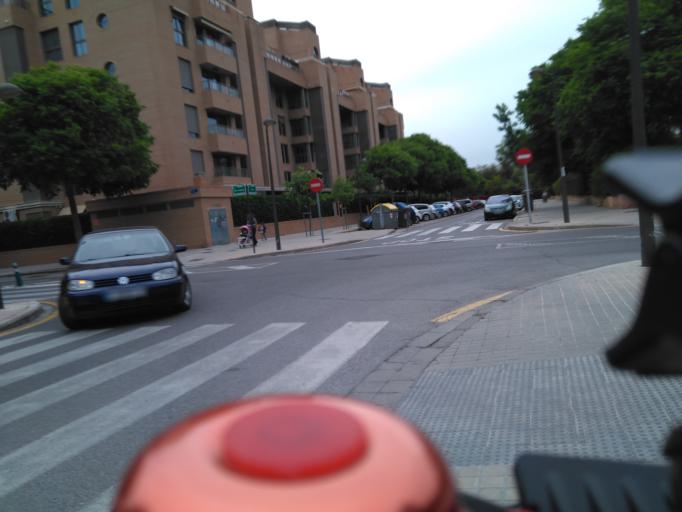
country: ES
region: Valencia
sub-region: Provincia de Valencia
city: Mislata
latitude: 39.4909
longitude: -0.4046
